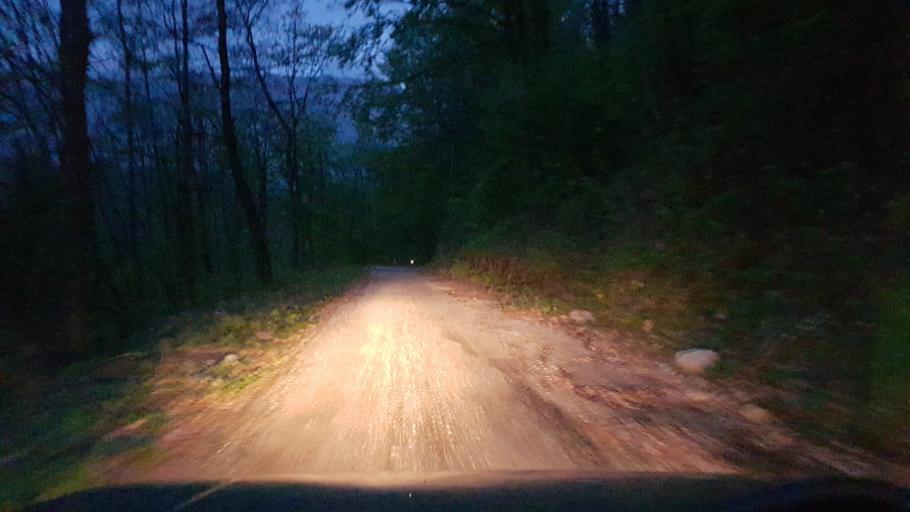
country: IT
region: Friuli Venezia Giulia
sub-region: Provincia di Udine
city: Taipana
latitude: 46.2482
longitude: 13.3564
